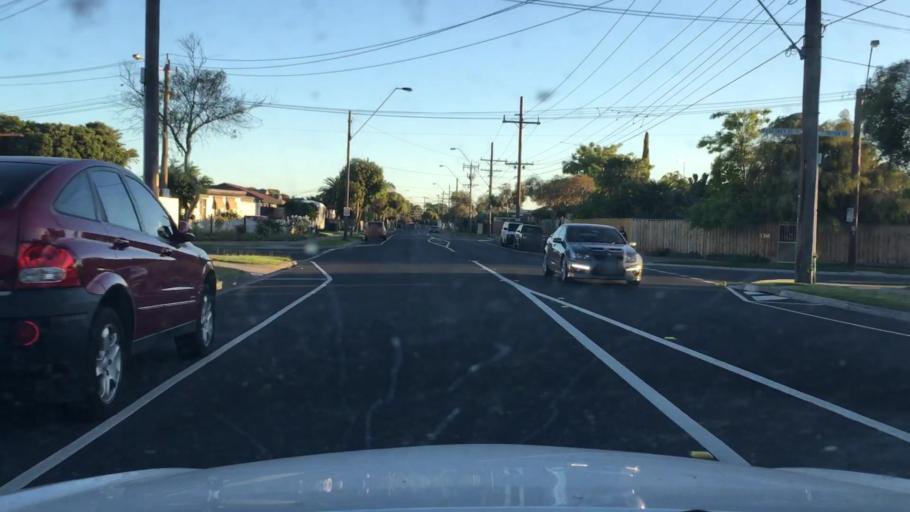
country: AU
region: Victoria
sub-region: Greater Dandenong
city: Keysborough
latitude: -37.9874
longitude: 145.1698
